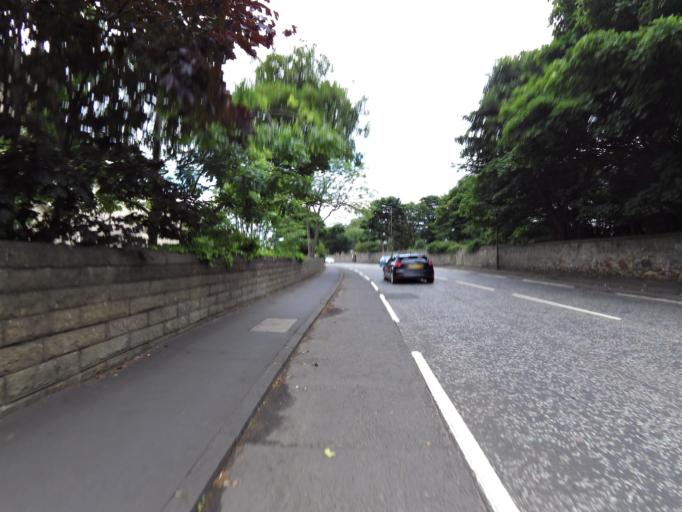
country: GB
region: Scotland
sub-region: East Lothian
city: Musselburgh
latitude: 55.9459
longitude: -3.0779
